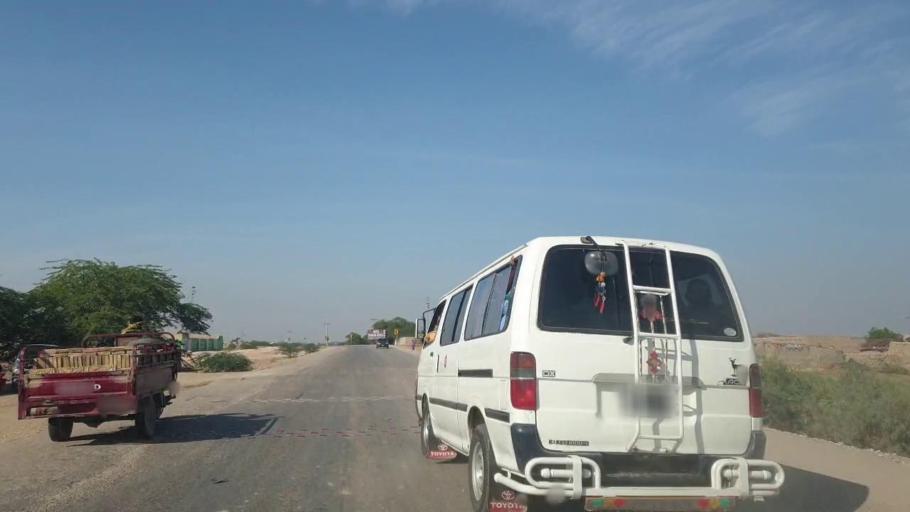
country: PK
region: Sindh
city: Sehwan
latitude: 26.3847
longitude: 67.8709
